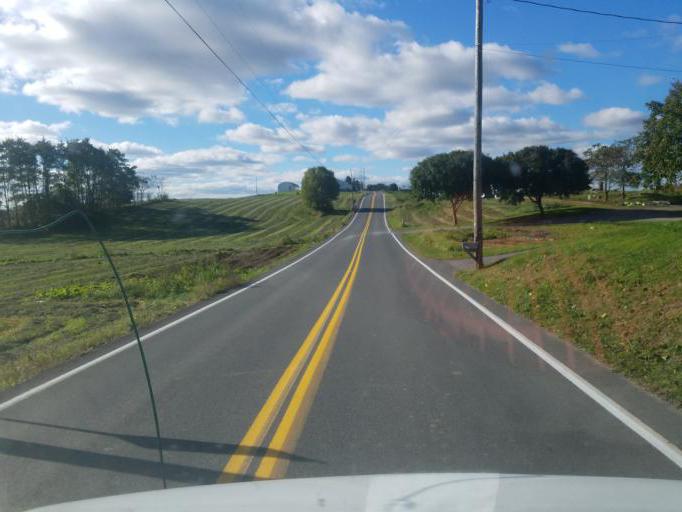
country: US
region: Pennsylvania
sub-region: Franklin County
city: Guilford Siding
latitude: 39.8247
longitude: -77.6387
